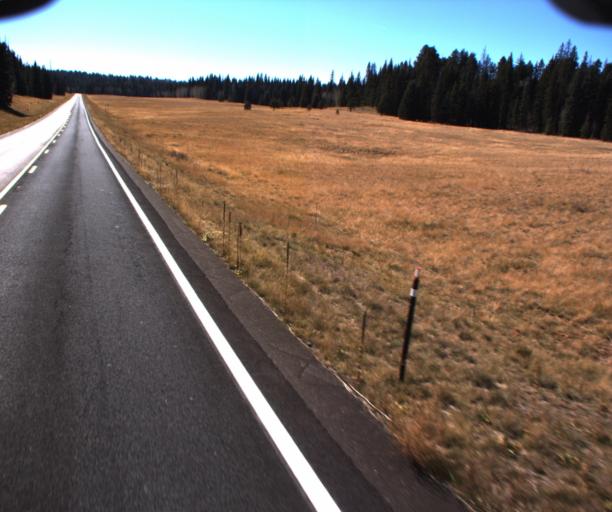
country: US
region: Arizona
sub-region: Coconino County
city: Grand Canyon
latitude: 36.4700
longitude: -112.1257
